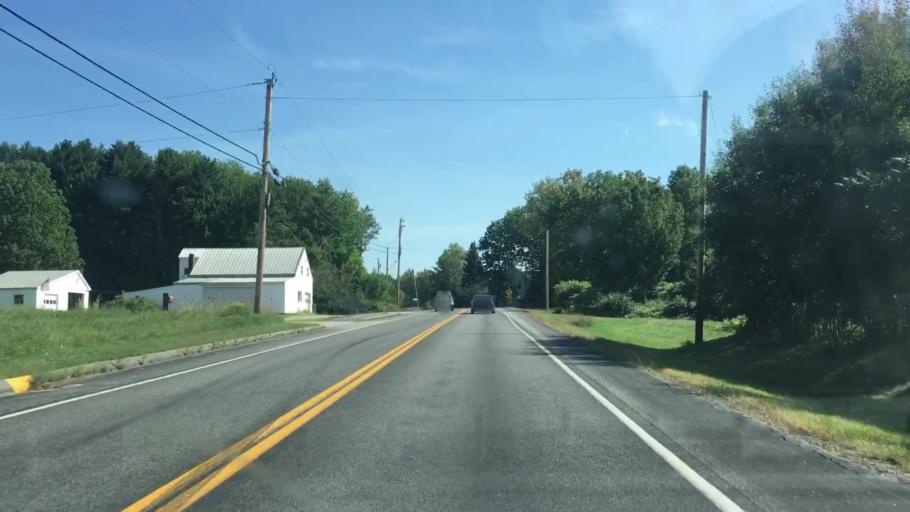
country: US
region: Maine
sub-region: Androscoggin County
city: Lisbon
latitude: 44.0356
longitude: -70.0721
